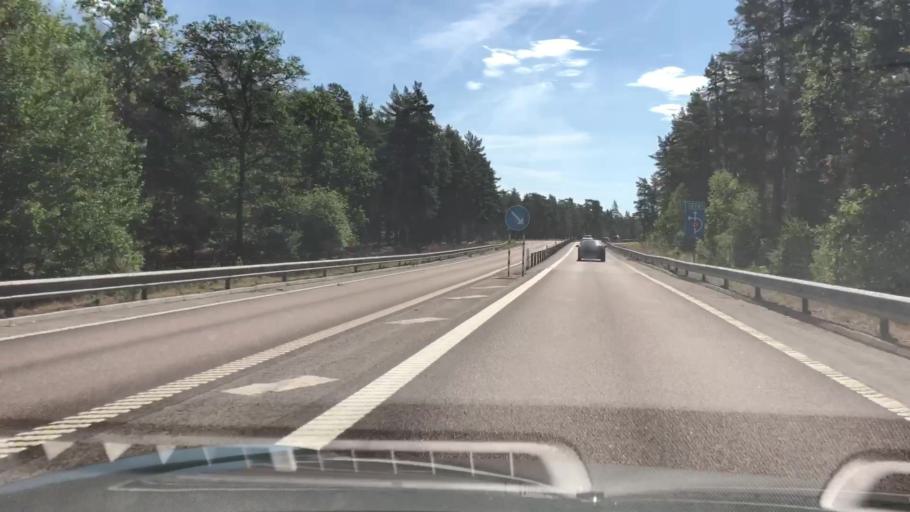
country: SE
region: Kalmar
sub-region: Oskarshamns Kommun
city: Paskallavik
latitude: 57.1257
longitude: 16.4851
